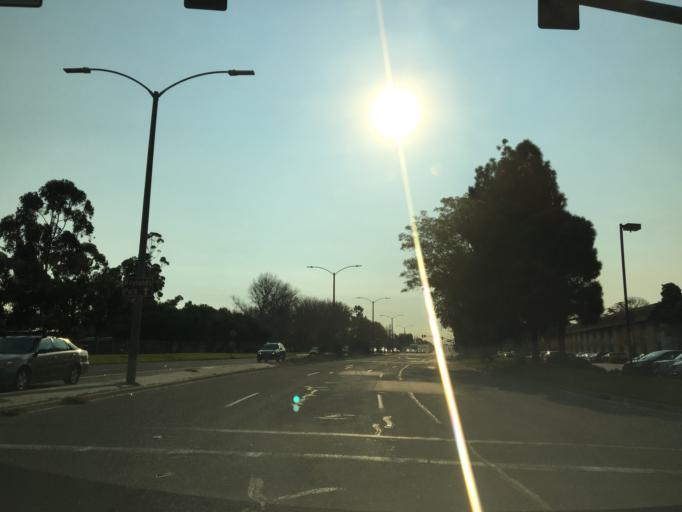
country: US
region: California
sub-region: Santa Clara County
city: Sunnyvale
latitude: 37.4139
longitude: -122.0019
